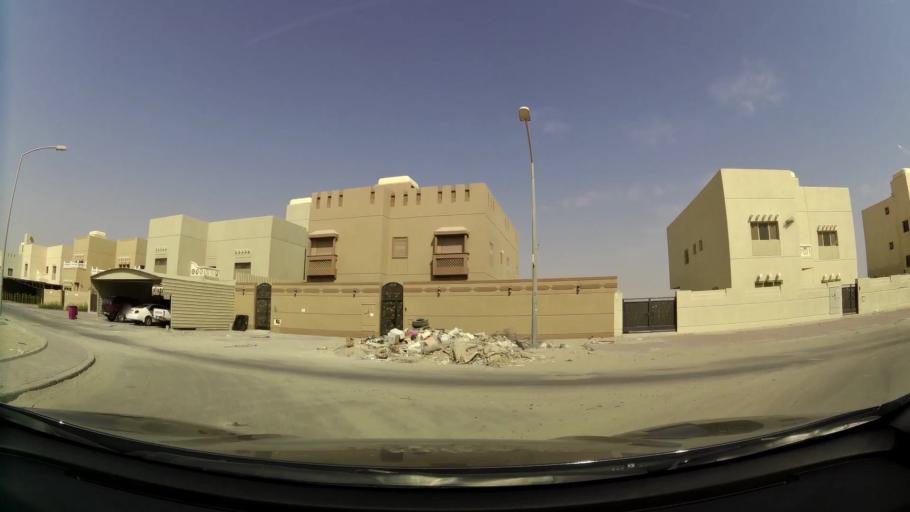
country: KW
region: Al Ahmadi
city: Al Wafrah
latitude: 28.8107
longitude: 48.0597
